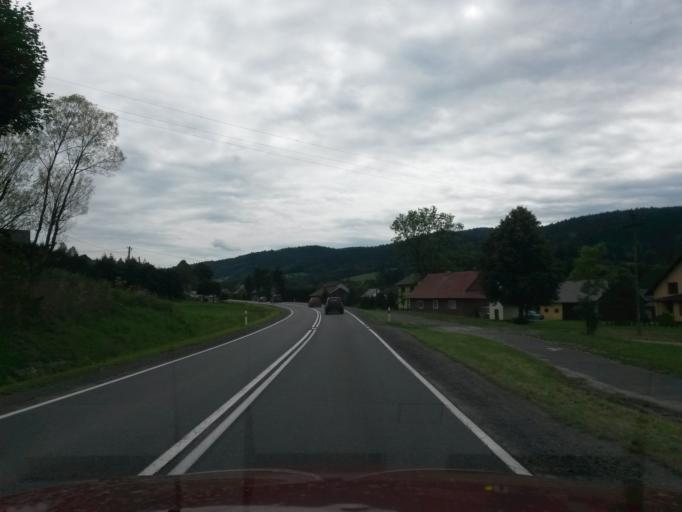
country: PL
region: Lesser Poland Voivodeship
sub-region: Powiat nowosadecki
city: Labowa
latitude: 49.5155
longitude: 20.8830
